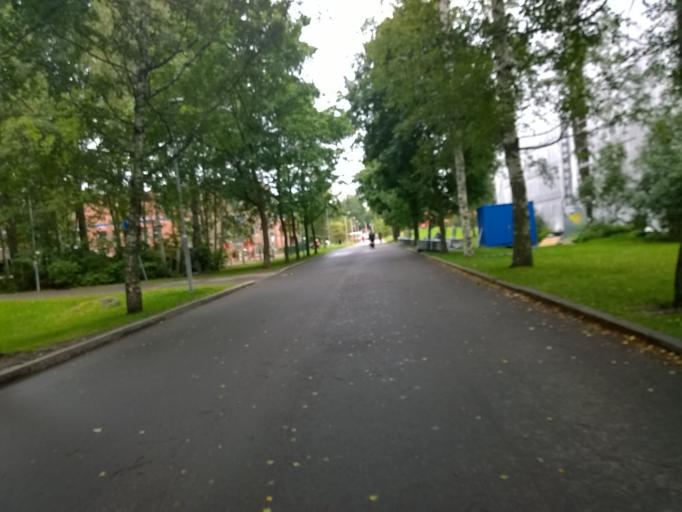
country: FI
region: Pirkanmaa
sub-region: Tampere
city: Tampere
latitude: 61.4490
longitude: 23.8484
